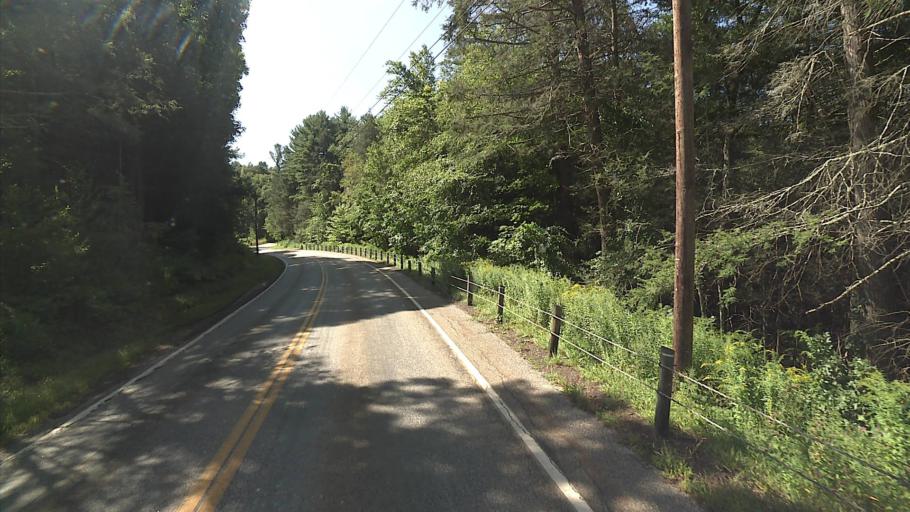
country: US
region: Connecticut
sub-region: Litchfield County
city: Plymouth
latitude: 41.7049
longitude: -73.0549
